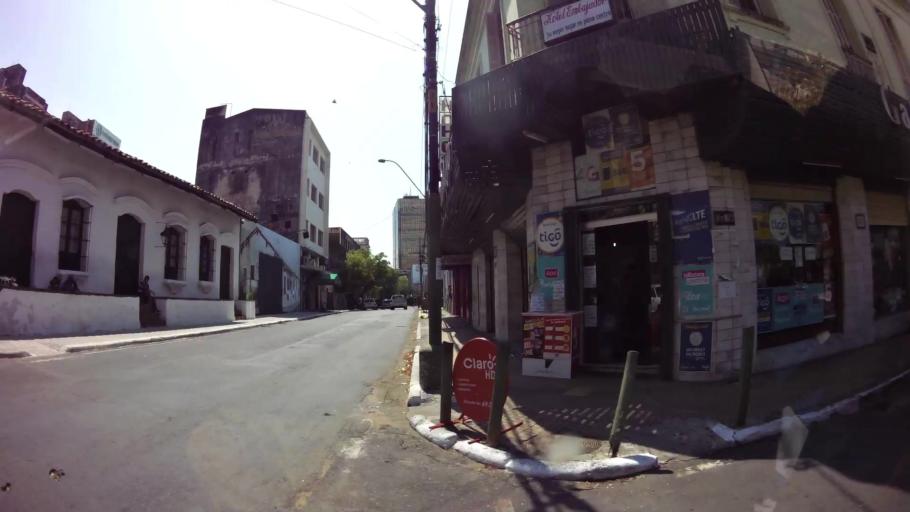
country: PY
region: Asuncion
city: Asuncion
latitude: -25.2805
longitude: -57.6360
